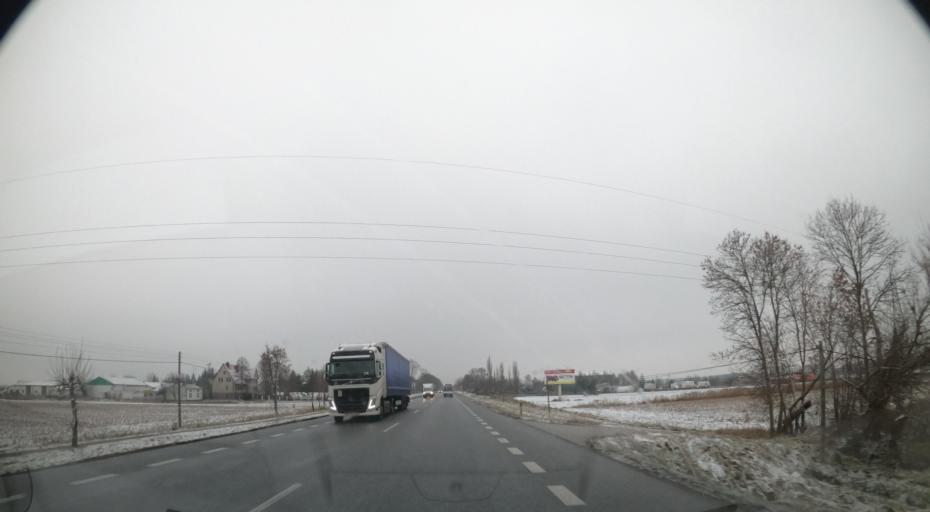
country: PL
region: Masovian Voivodeship
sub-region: Powiat warszawski zachodni
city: Bieniewice
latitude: 52.2000
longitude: 20.5829
